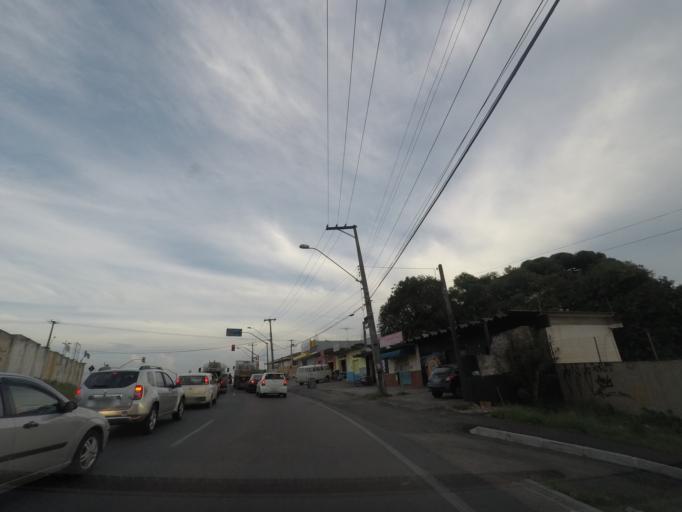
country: BR
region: Parana
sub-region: Curitiba
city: Curitiba
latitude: -25.3737
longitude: -49.2231
